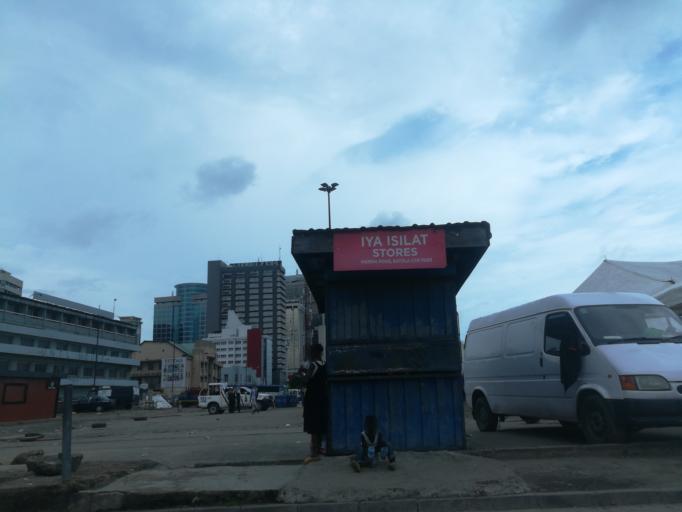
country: NG
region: Lagos
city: Lagos
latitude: 6.4546
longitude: 3.3834
